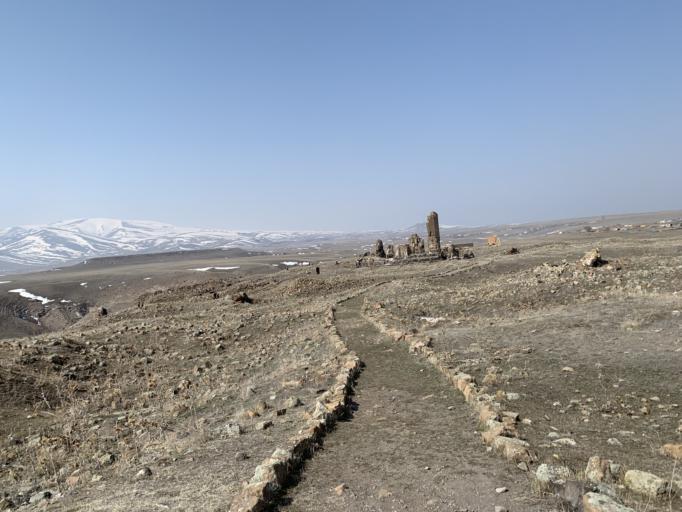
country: TR
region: Kars
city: Basgedikler
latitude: 40.5094
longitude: 43.5703
